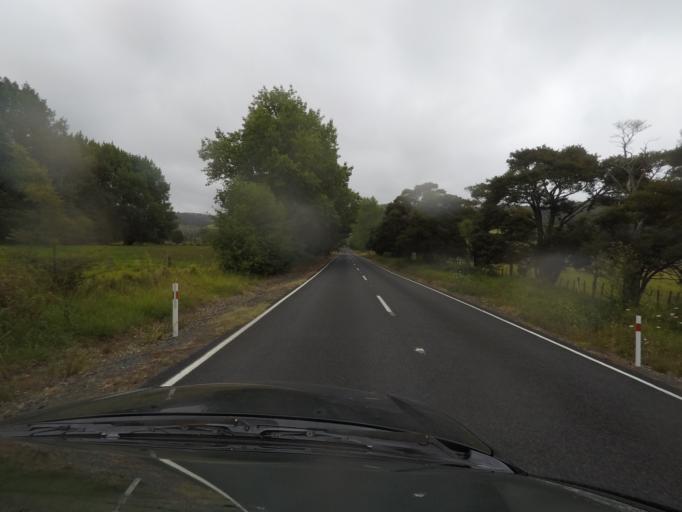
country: NZ
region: Auckland
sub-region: Auckland
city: Warkworth
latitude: -36.2642
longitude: 174.7029
